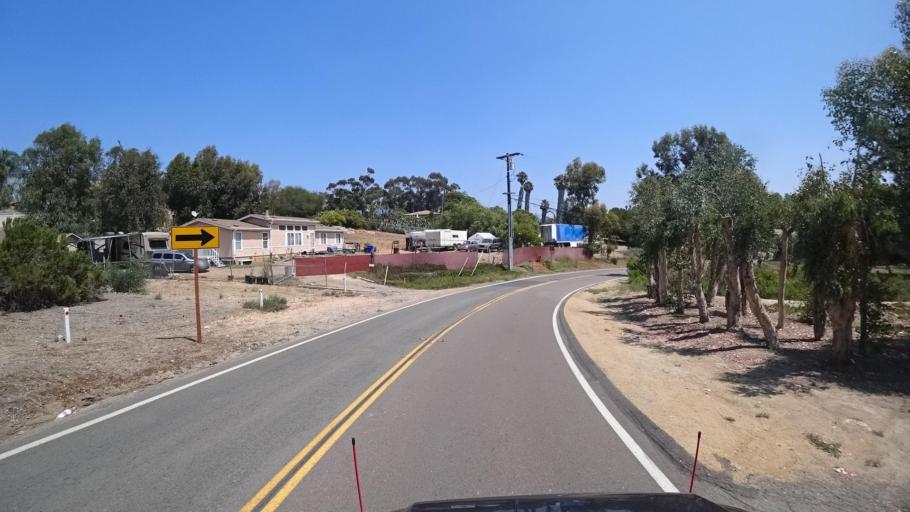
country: US
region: California
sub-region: San Diego County
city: Vista
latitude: 33.1826
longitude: -117.2684
